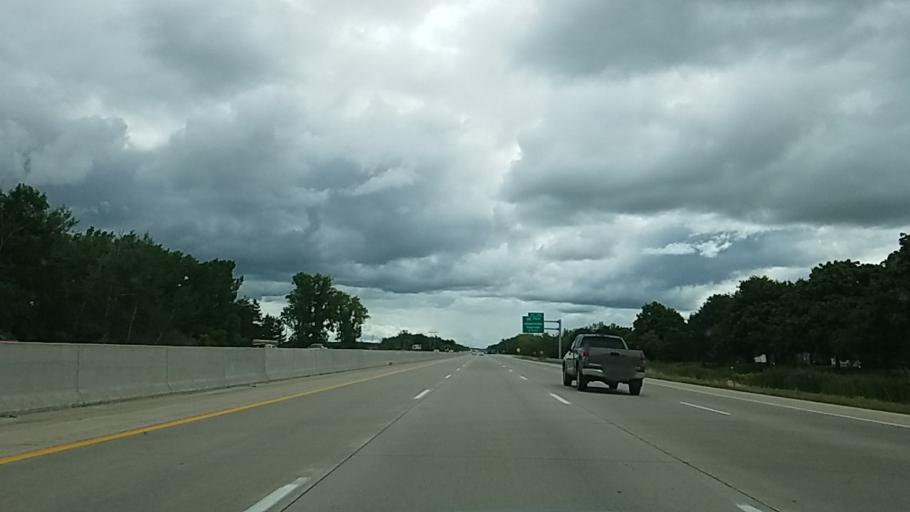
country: US
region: Michigan
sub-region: Saginaw County
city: Zilwaukee
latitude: 43.5294
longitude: -83.9428
